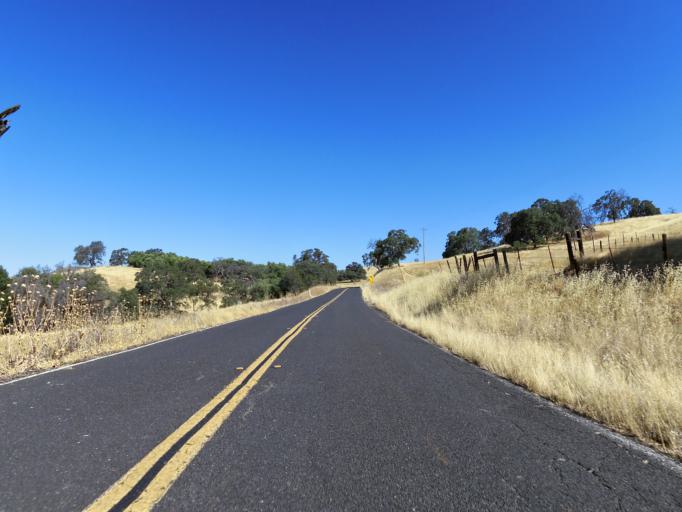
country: US
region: California
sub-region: Mariposa County
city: Mariposa
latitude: 37.4954
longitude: -120.1578
